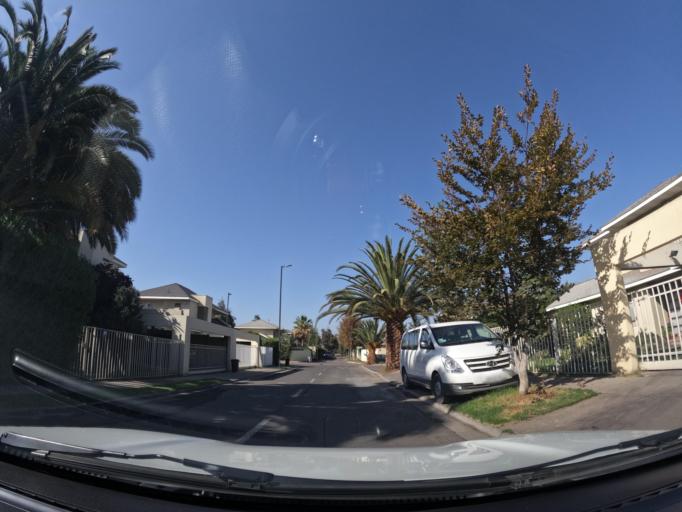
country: CL
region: Santiago Metropolitan
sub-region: Provincia de Santiago
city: Villa Presidente Frei, Nunoa, Santiago, Chile
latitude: -33.4905
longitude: -70.5518
